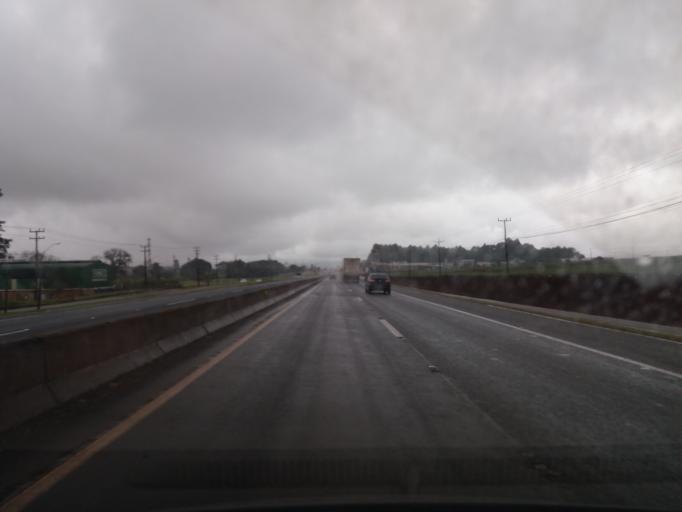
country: BR
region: Parana
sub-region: Cascavel
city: Cascavel
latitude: -24.9928
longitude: -53.5117
